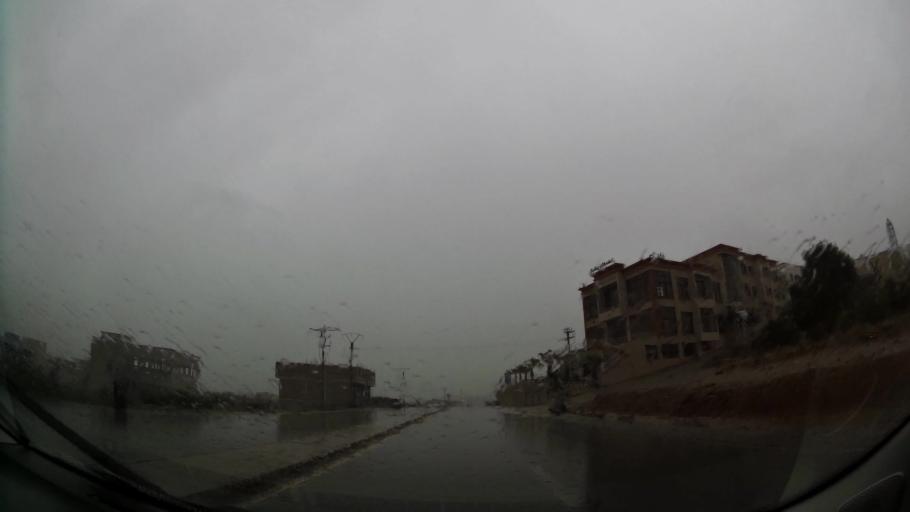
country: MA
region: Taza-Al Hoceima-Taounate
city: Imzourene
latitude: 35.1330
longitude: -3.8464
